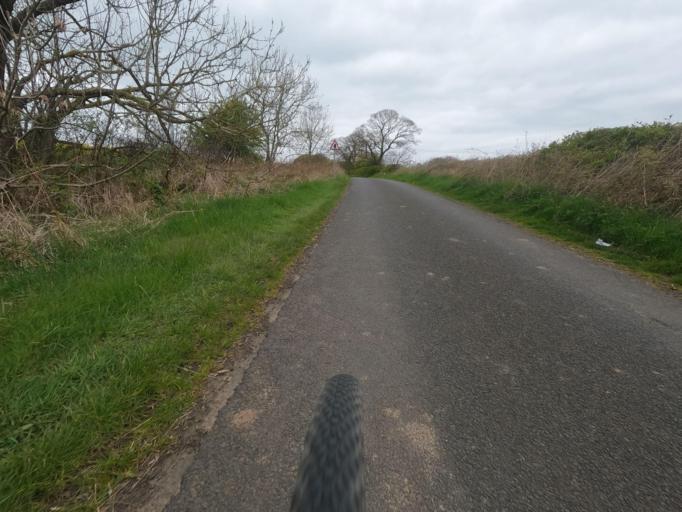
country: GB
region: England
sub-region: Northumberland
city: Horsley
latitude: 55.0593
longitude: -1.8450
